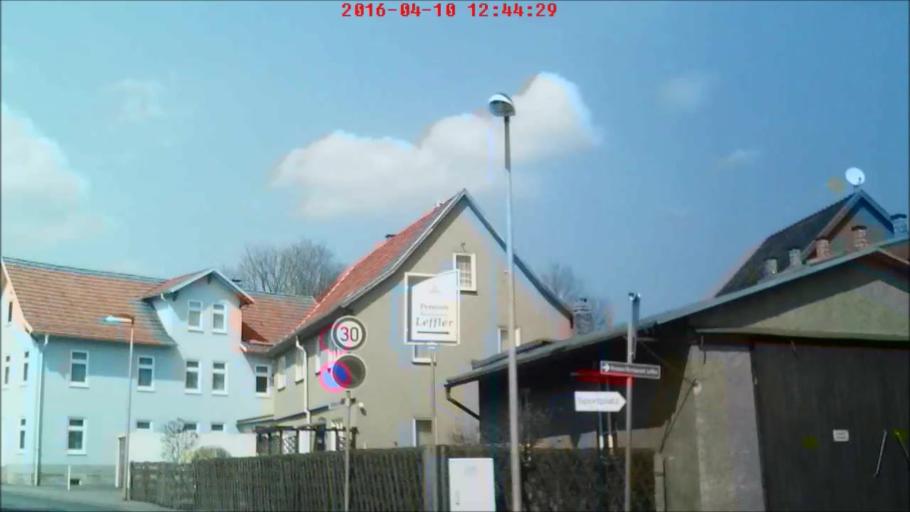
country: DE
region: Thuringia
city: Pappenheim
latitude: 50.7637
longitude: 10.4747
